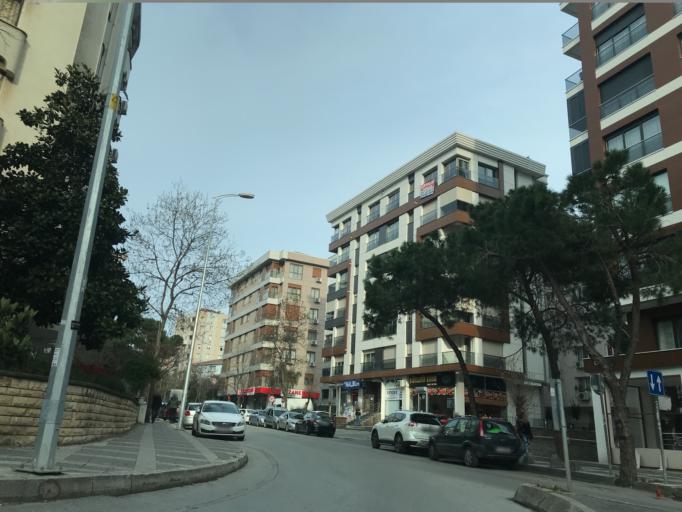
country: TR
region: Istanbul
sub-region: Atasehir
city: Atasehir
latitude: 40.9626
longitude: 29.0970
